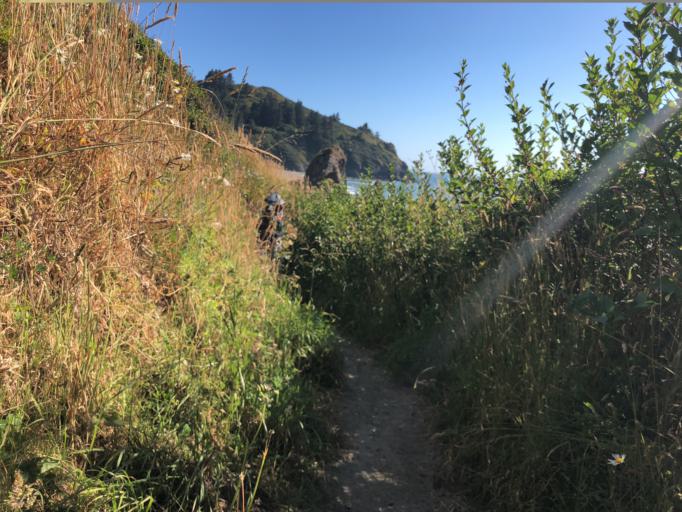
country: US
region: California
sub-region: Humboldt County
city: Westhaven-Moonstone
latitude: 41.0617
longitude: -124.1480
